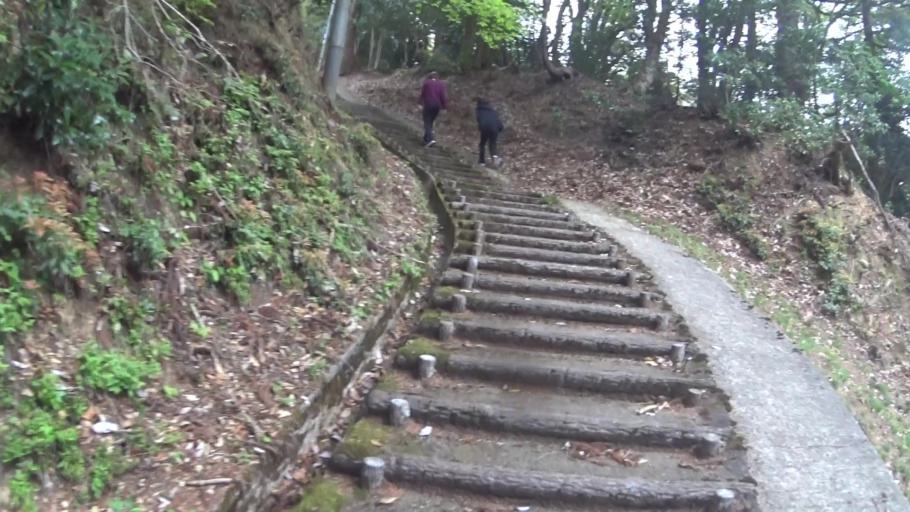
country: JP
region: Kyoto
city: Maizuru
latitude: 35.3880
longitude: 135.4428
